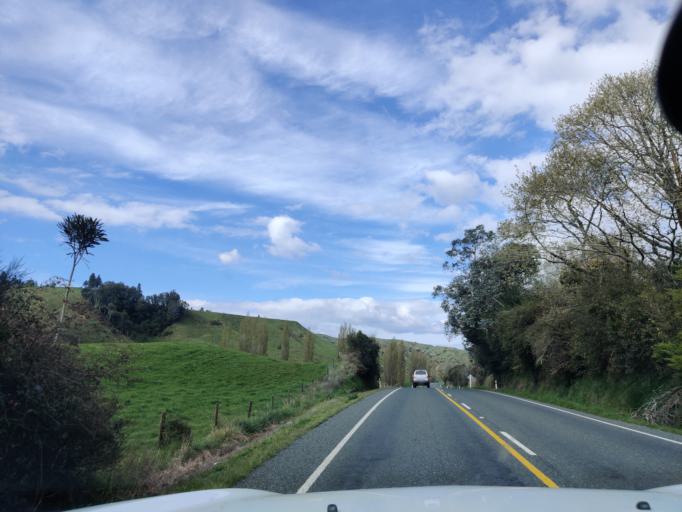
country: NZ
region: Waikato
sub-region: Otorohanga District
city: Otorohanga
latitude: -38.5201
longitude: 175.1872
